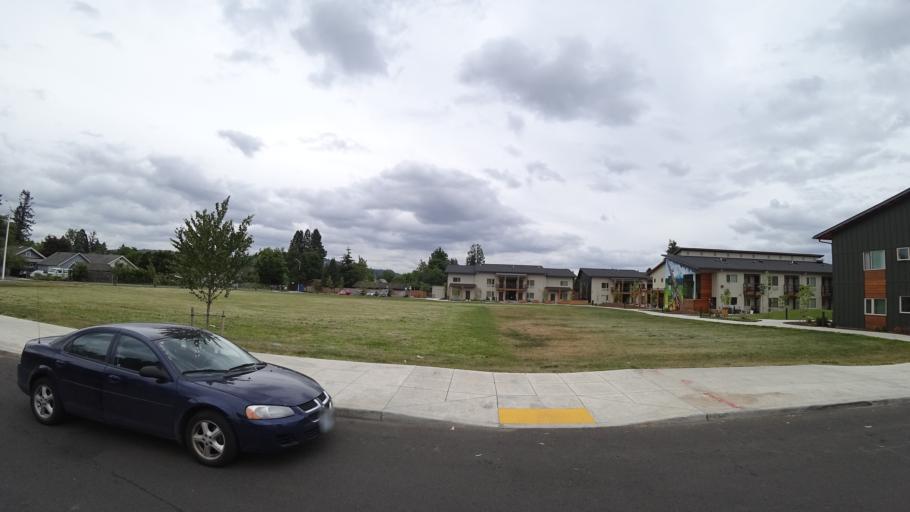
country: US
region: Oregon
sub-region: Multnomah County
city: Lents
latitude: 45.4849
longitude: -122.5749
